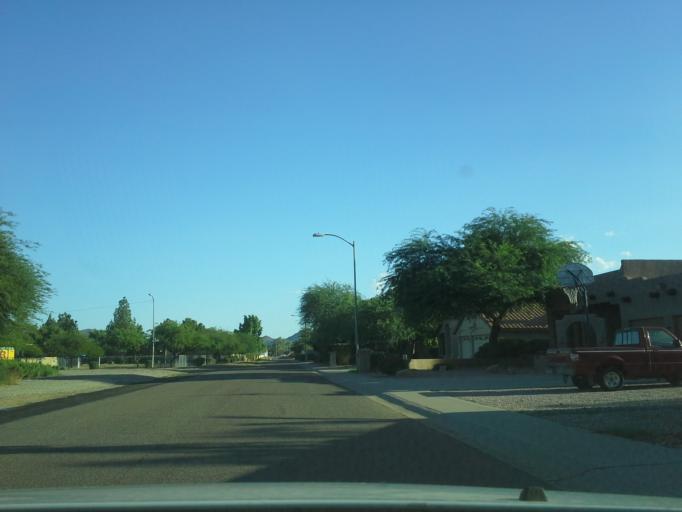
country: US
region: Arizona
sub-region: Maricopa County
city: Paradise Valley
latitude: 33.6159
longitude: -112.0155
